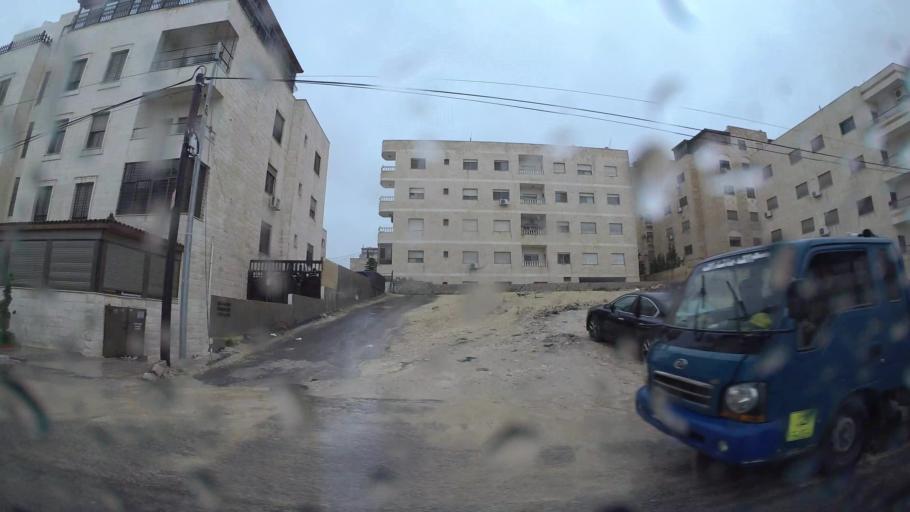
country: JO
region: Amman
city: Al Jubayhah
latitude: 32.0264
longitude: 35.8892
